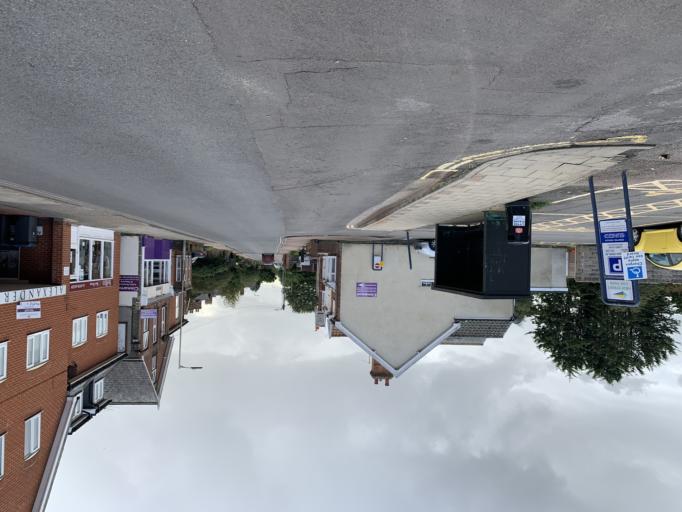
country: GB
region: England
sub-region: Suffolk
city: Leiston
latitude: 52.2052
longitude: 1.5780
